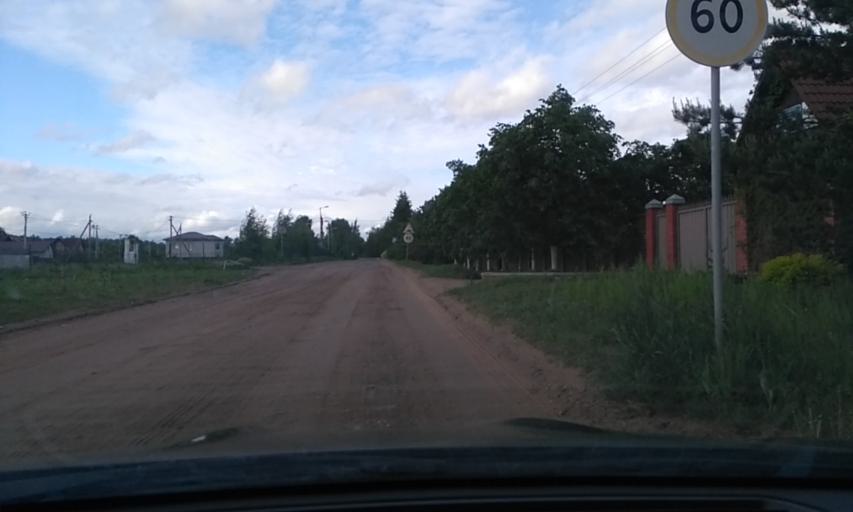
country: RU
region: Leningrad
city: Otradnoye
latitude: 59.7935
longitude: 30.7961
